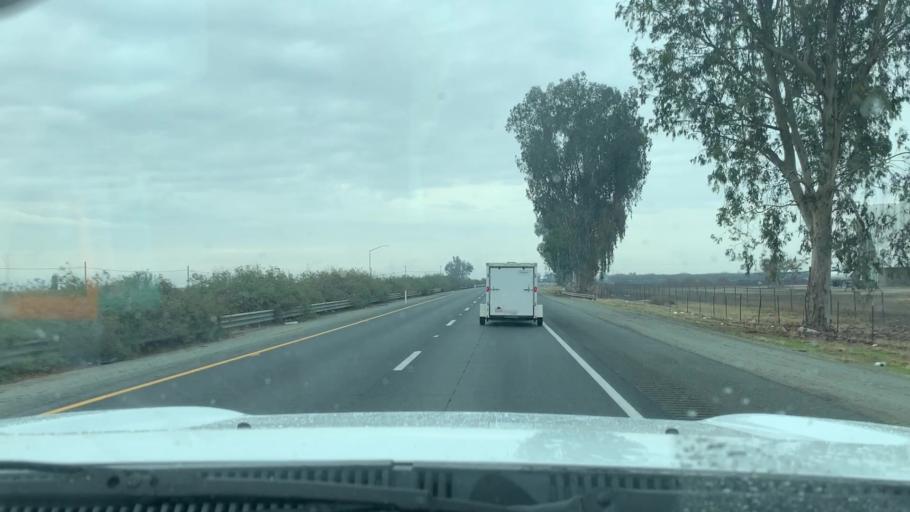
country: US
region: California
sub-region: Kern County
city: Delano
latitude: 35.8149
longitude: -119.2580
